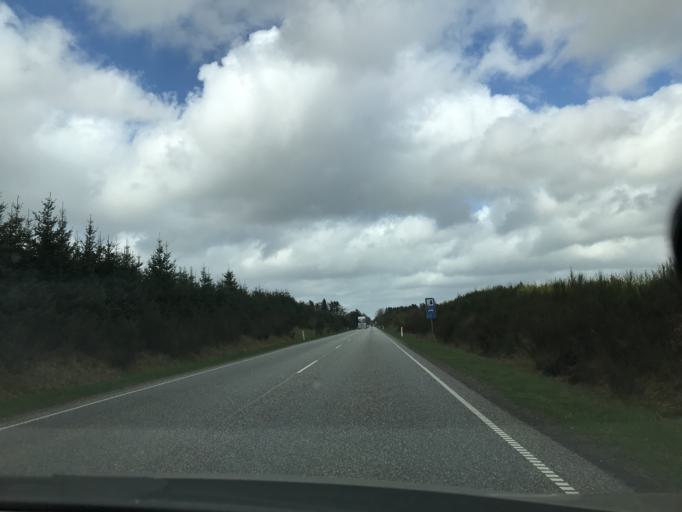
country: DK
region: Central Jutland
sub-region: Herning Kommune
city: Sunds
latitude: 56.3776
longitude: 8.9866
